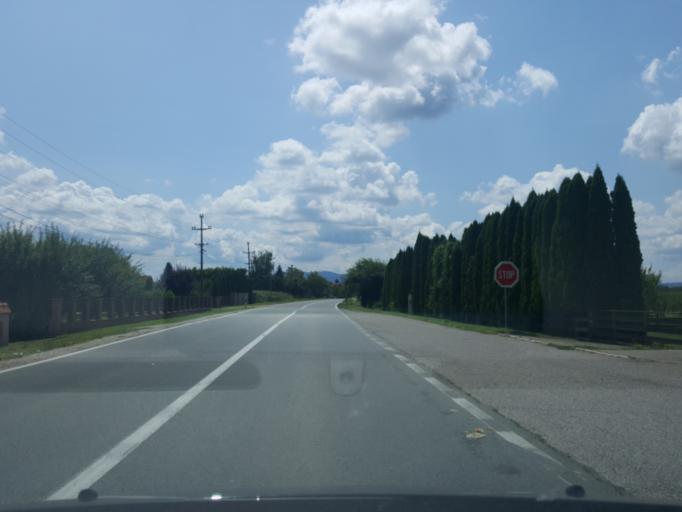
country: RS
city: Lesnica
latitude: 44.6391
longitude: 19.2783
